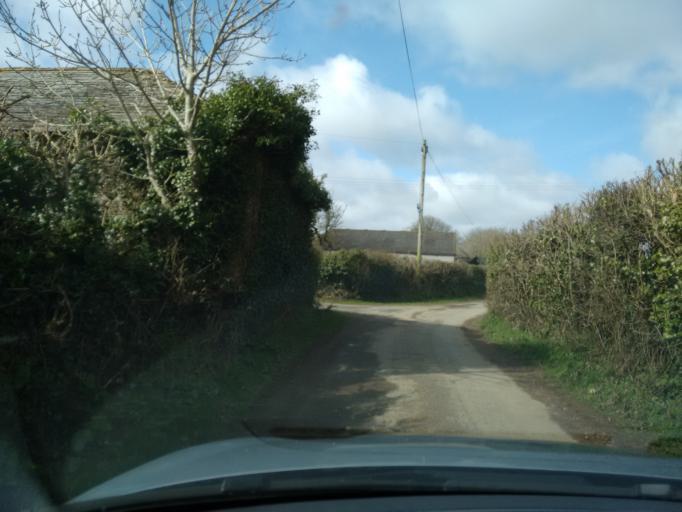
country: GB
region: England
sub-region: Cornwall
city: Launceston
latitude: 50.5975
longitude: -4.3586
